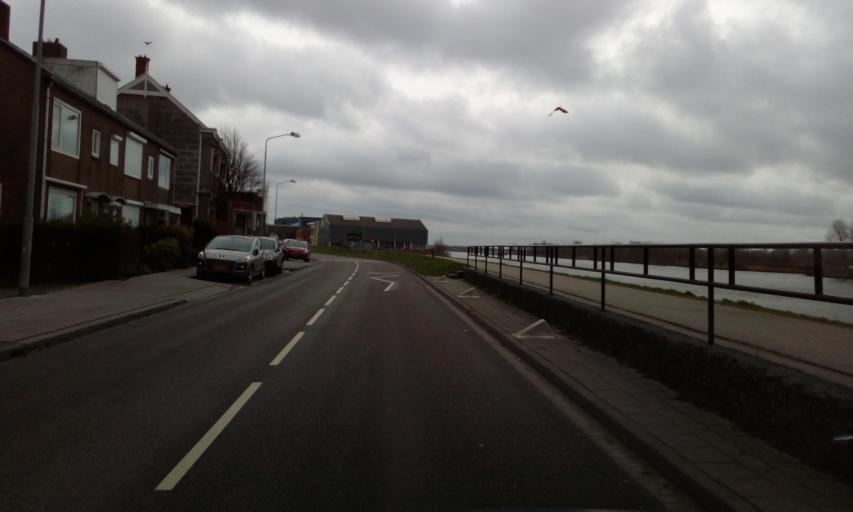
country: NL
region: South Holland
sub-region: Gemeente Ridderkerk
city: Ridderkerk
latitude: 51.8799
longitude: 4.6287
